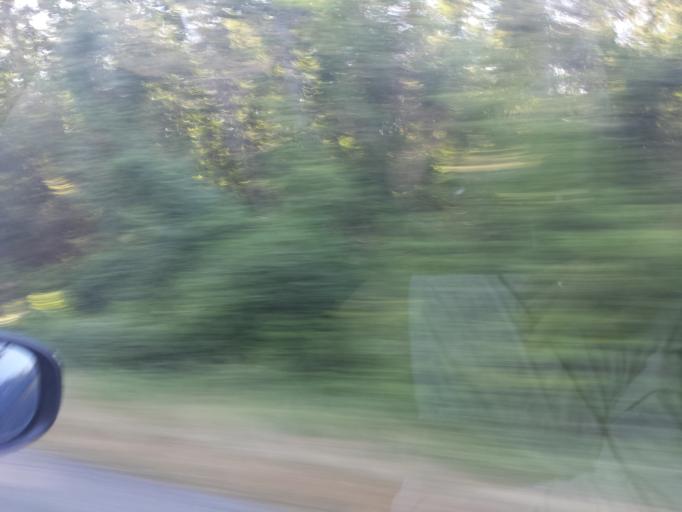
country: RO
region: Ialomita
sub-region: Comuna Slobozia
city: Slobozia
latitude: 44.5750
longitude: 27.3995
